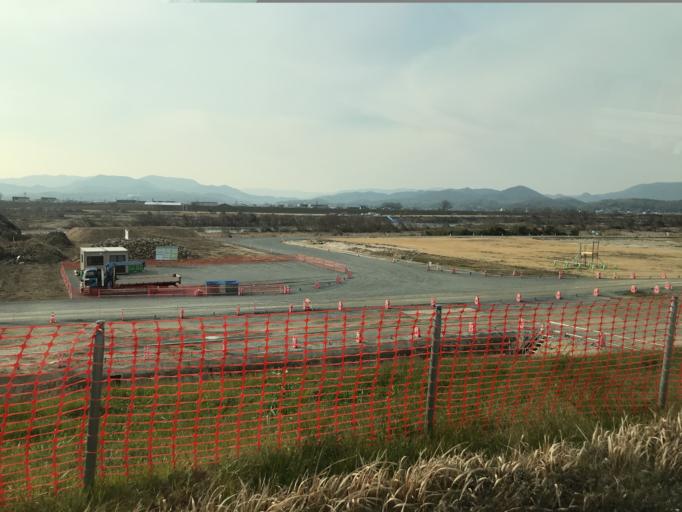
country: JP
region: Okayama
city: Soja
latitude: 34.6366
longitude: 133.7309
